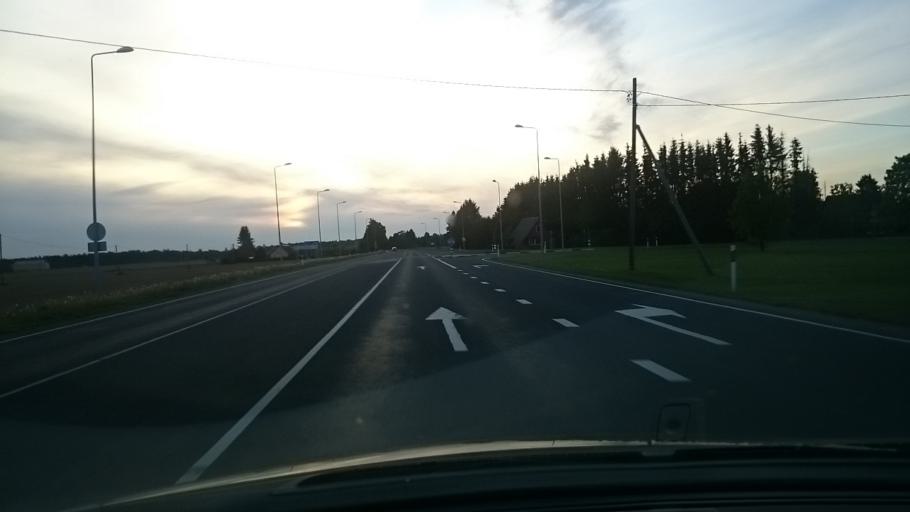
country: EE
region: Viljandimaa
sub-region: Vohma linn
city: Vohma
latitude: 58.7557
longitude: 25.5608
